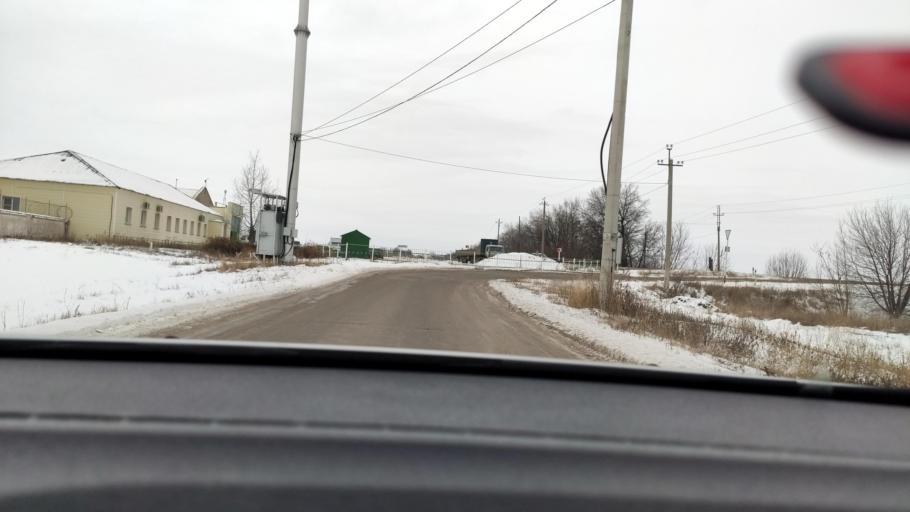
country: RU
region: Voronezj
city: Semiluki
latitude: 51.7226
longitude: 38.9948
